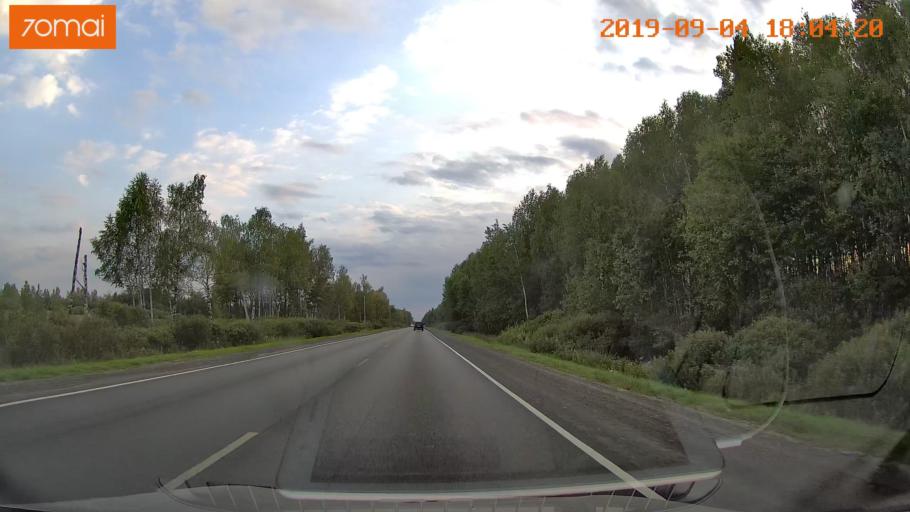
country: RU
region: Moskovskaya
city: Il'inskiy Pogost
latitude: 55.4535
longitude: 38.8405
